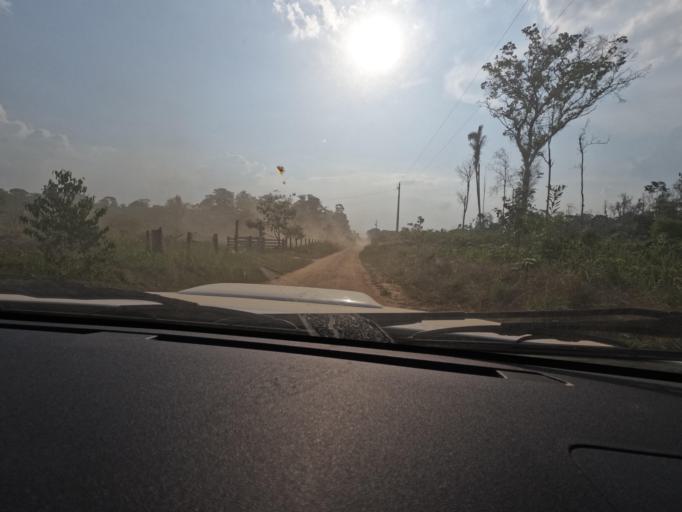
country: BR
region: Rondonia
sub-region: Porto Velho
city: Porto Velho
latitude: -8.5652
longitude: -64.0245
